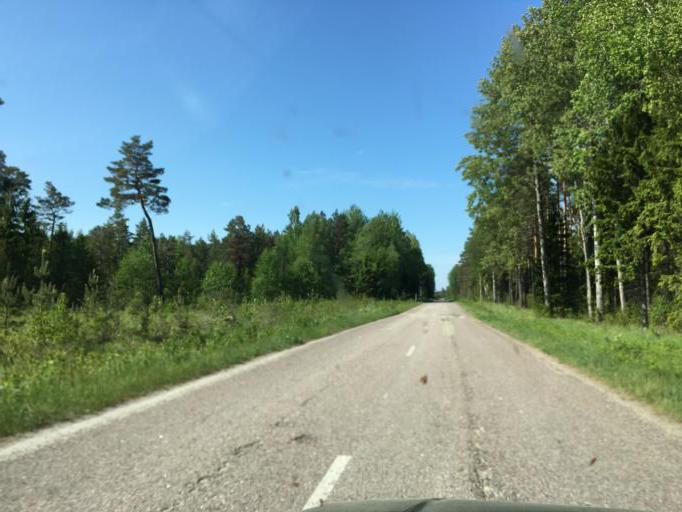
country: LV
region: Ventspils
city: Ventspils
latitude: 57.4891
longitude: 21.7864
